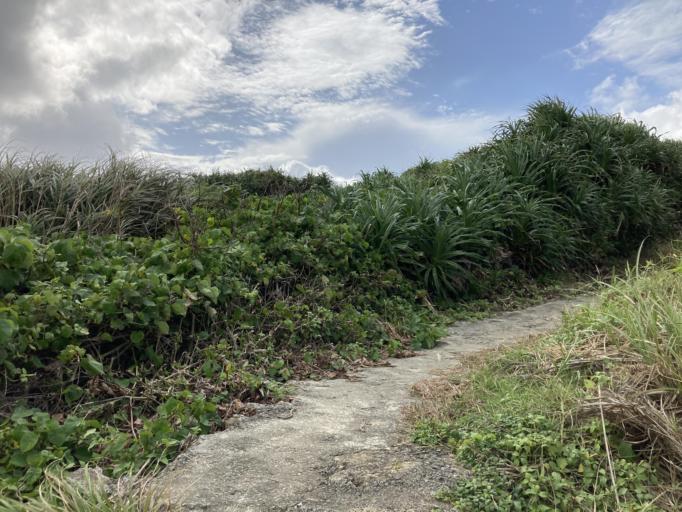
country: JP
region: Okinawa
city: Itoman
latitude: 26.0771
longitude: 127.6820
